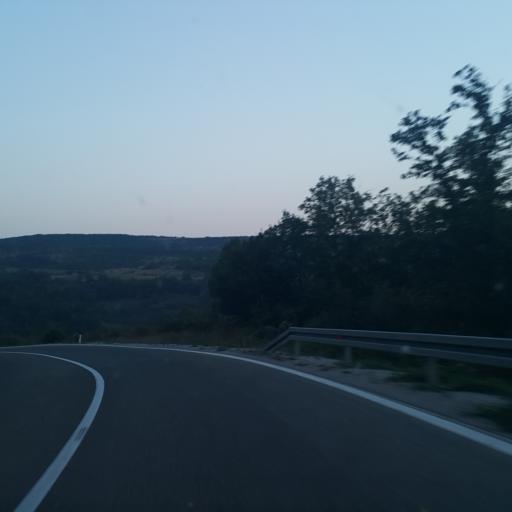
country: RS
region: Central Serbia
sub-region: Nisavski Okrug
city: Svrljig
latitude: 43.4519
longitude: 22.1801
